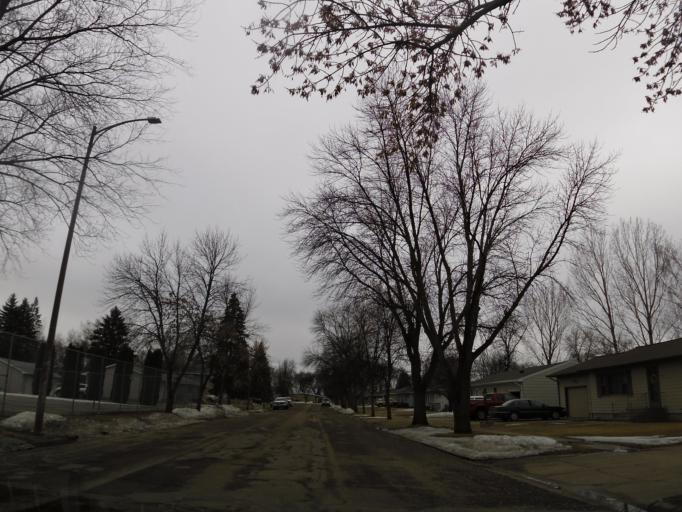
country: US
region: North Dakota
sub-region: Walsh County
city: Grafton
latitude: 48.4106
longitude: -97.4189
